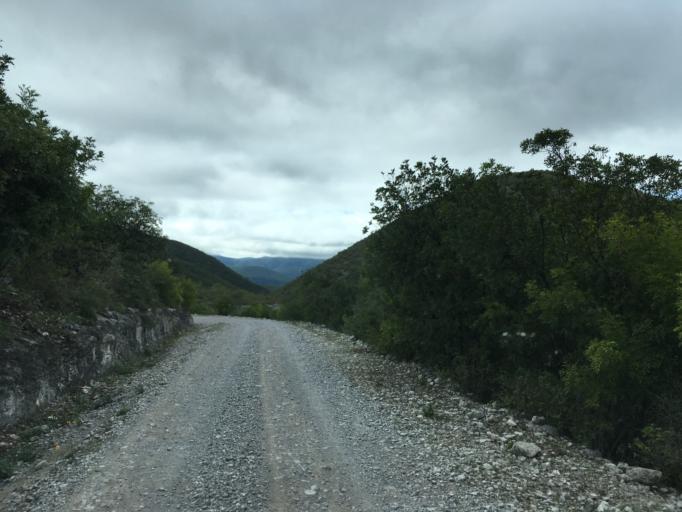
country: MX
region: Hidalgo
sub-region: Metztitlan
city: Fontezuelas
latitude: 20.6237
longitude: -98.8634
